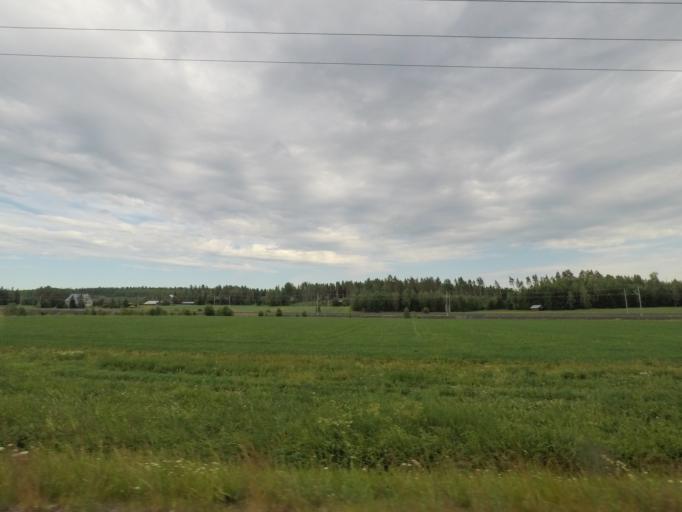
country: FI
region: Uusimaa
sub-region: Helsinki
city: Maentsaelae
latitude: 60.6843
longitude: 25.3674
